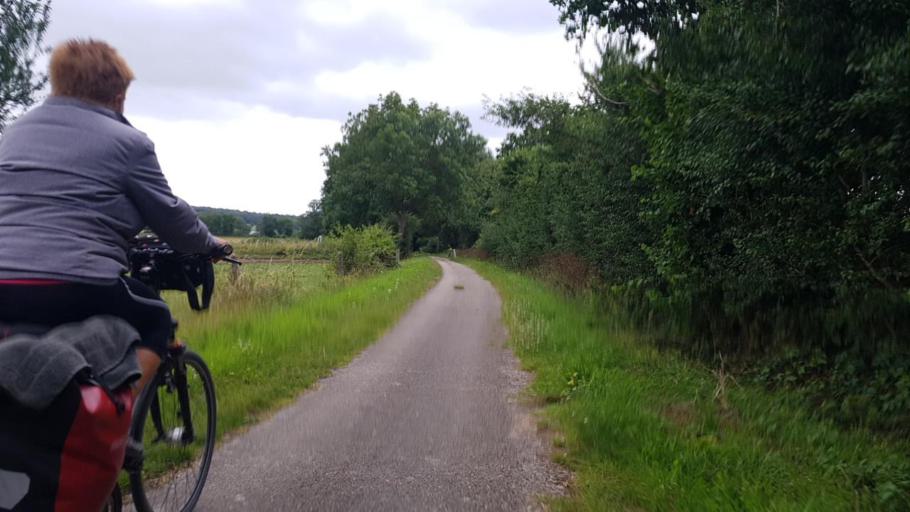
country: FR
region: Picardie
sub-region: Departement de l'Aisne
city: Buironfosse
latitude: 49.9030
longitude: 3.8435
